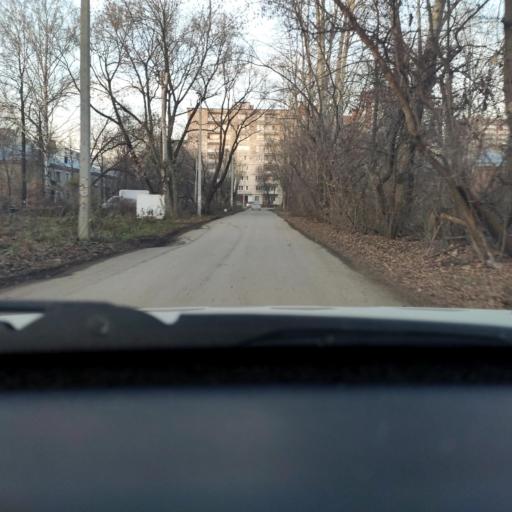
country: RU
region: Perm
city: Perm
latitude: 57.9621
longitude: 56.2357
